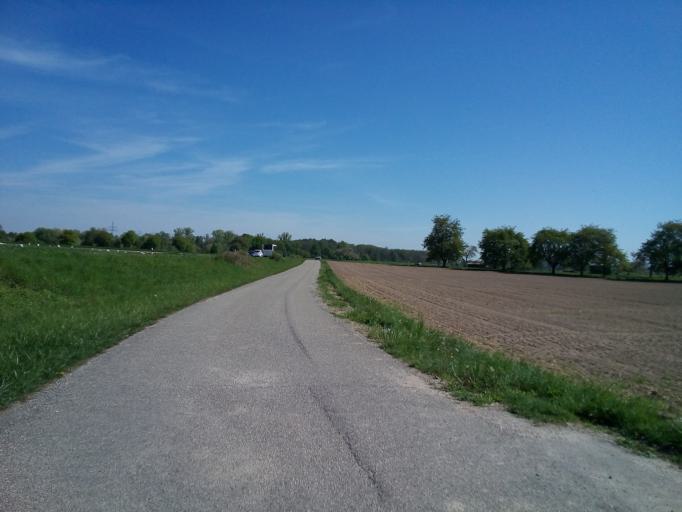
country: DE
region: Baden-Wuerttemberg
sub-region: Freiburg Region
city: Rheinau
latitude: 48.6758
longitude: 7.9602
